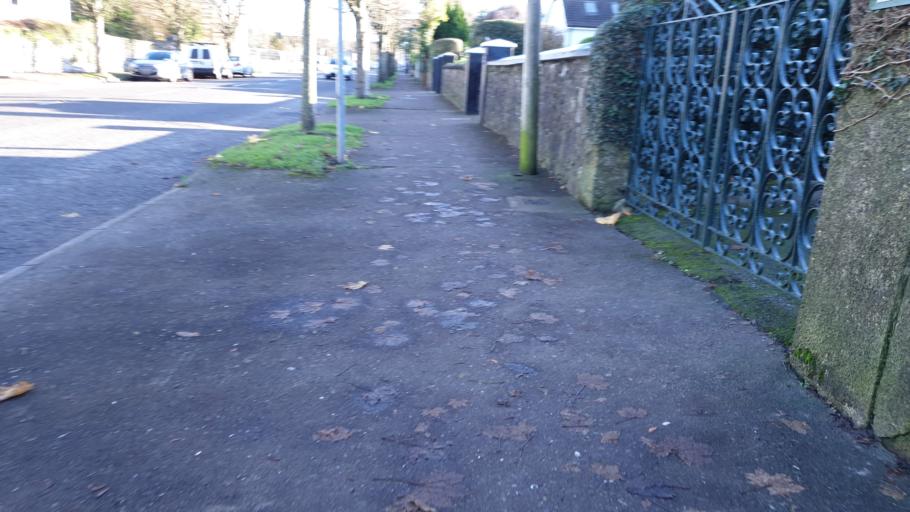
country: IE
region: Munster
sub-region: County Cork
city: Cork
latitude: 51.8912
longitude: -8.4502
